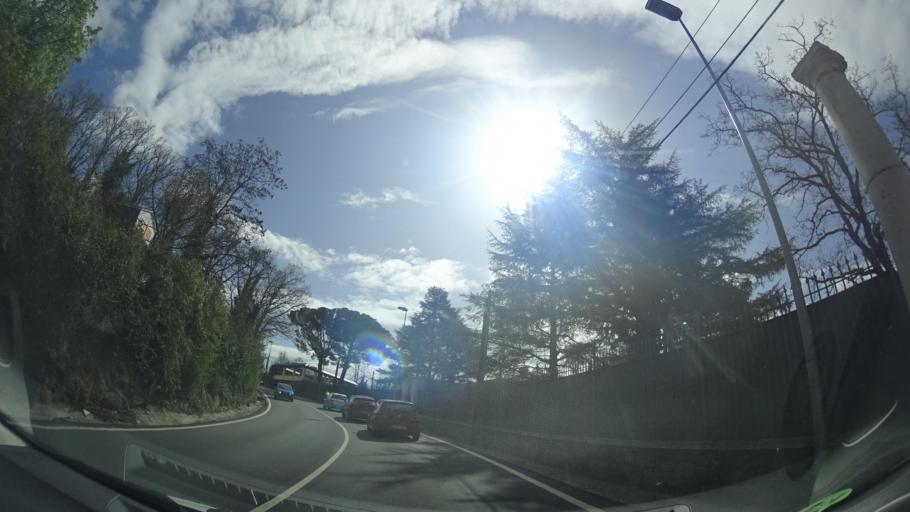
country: ES
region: Madrid
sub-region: Provincia de Madrid
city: Miraflores de la Sierra
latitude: 40.8100
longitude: -3.7709
